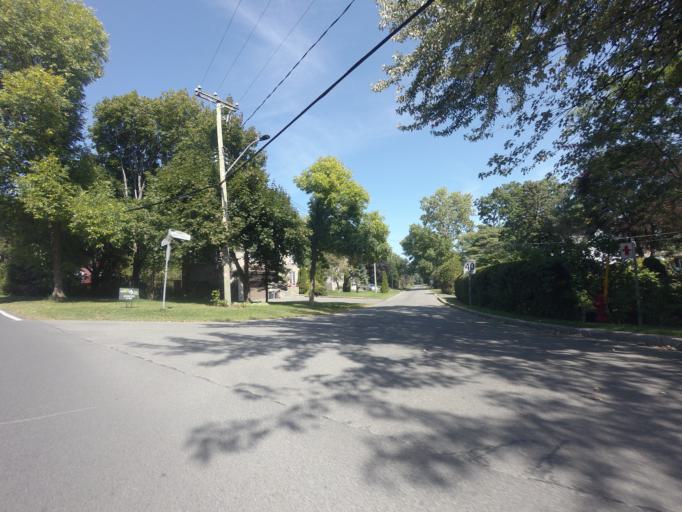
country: CA
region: Quebec
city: Dollard-Des Ormeaux
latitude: 45.5099
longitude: -73.8581
